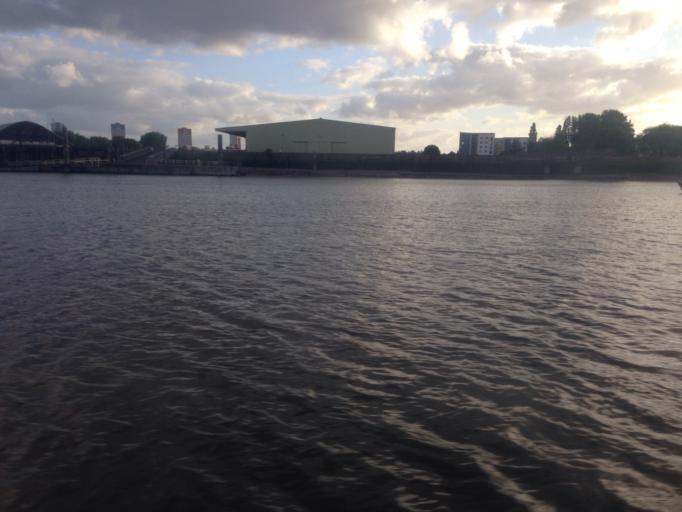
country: GB
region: England
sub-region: Greater London
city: Poplar
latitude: 51.4892
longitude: -0.0259
